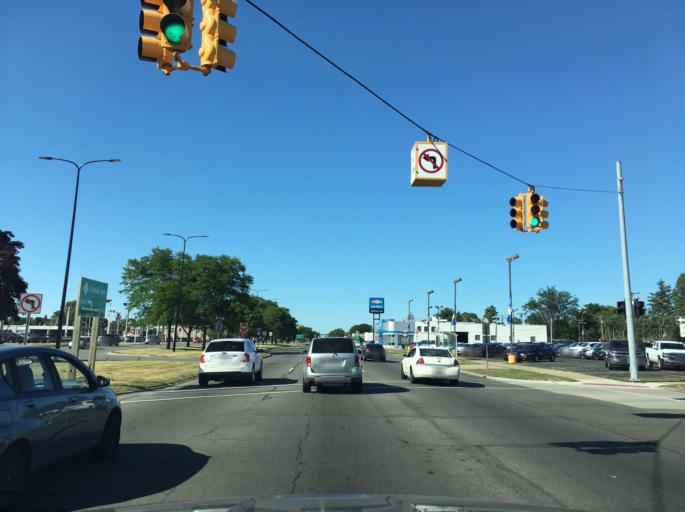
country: US
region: Michigan
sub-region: Macomb County
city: Eastpointe
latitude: 42.4573
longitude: -82.9627
